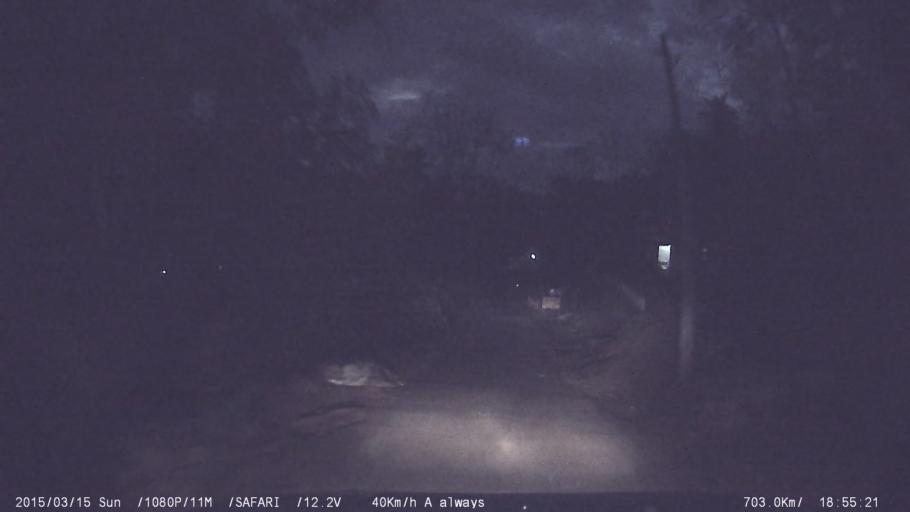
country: IN
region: Kerala
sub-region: Kottayam
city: Palackattumala
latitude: 9.8584
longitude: 76.6775
